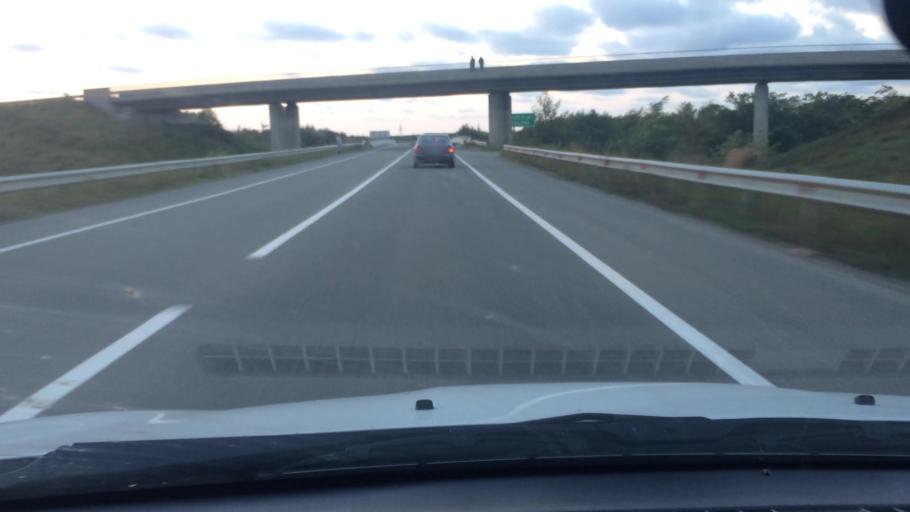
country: GE
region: Ajaria
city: Ochkhamuri
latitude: 41.8919
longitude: 41.8055
